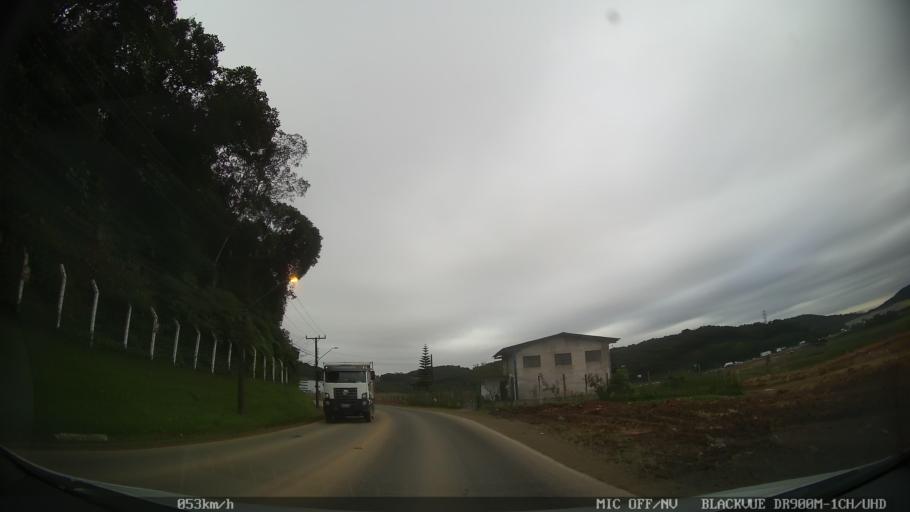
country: BR
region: Santa Catarina
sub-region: Joinville
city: Joinville
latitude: -26.2519
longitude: -48.9106
